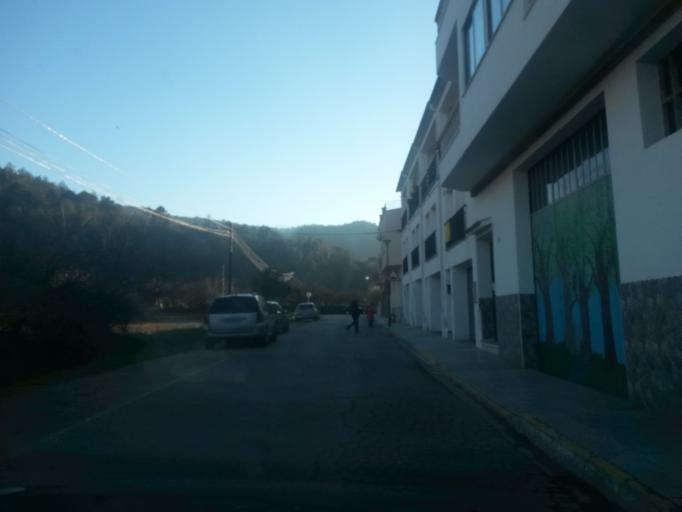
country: ES
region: Catalonia
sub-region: Provincia de Girona
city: Bescano
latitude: 41.9637
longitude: 2.7403
